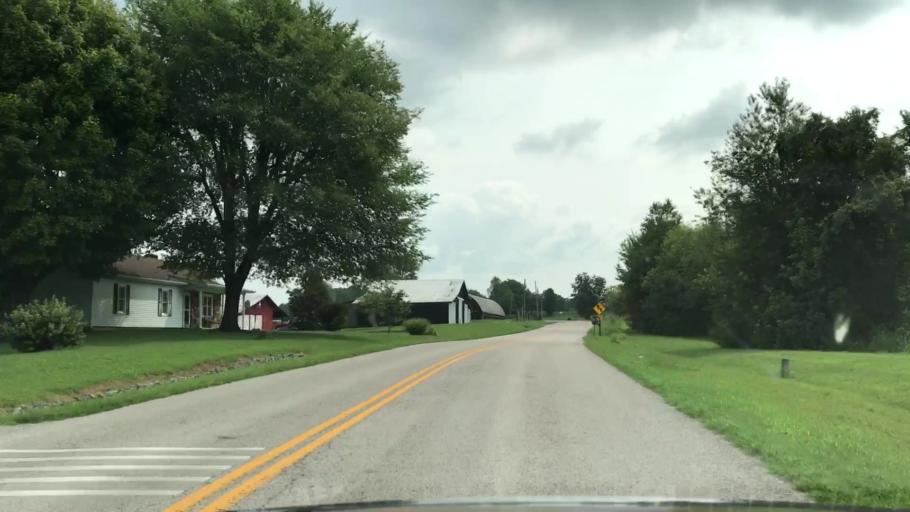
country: US
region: Kentucky
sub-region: Edmonson County
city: Brownsville
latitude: 37.1559
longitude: -86.2198
